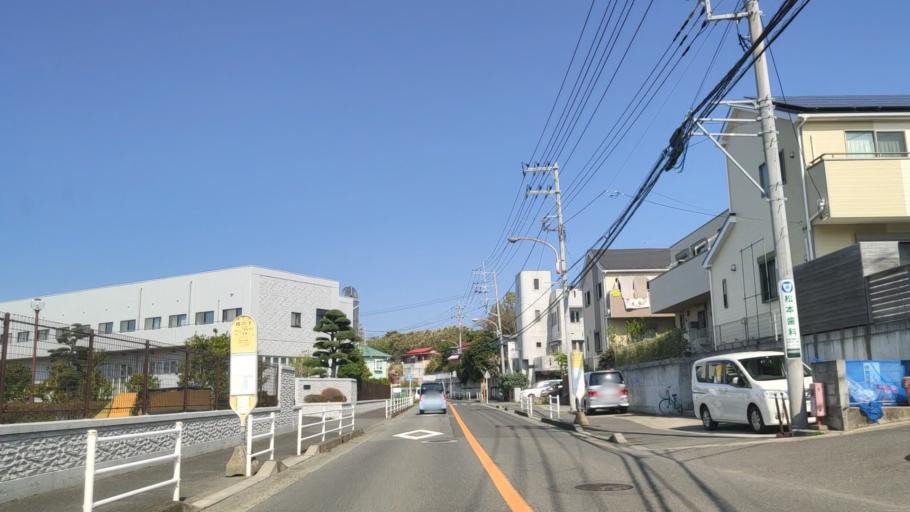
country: JP
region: Kanagawa
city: Oiso
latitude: 35.3084
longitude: 139.2874
